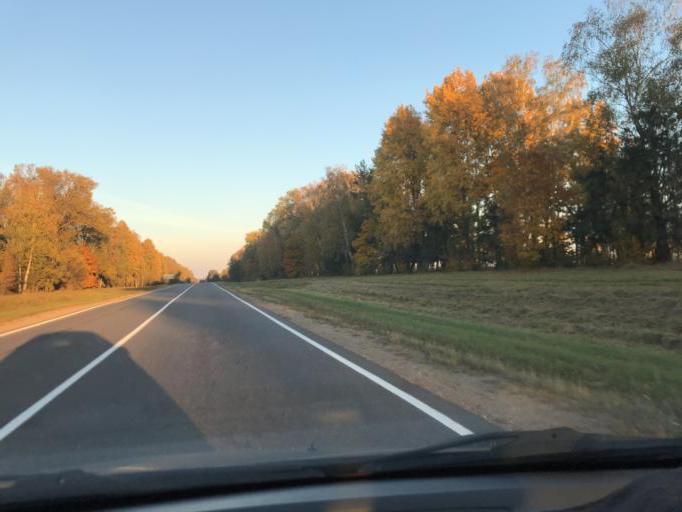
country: BY
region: Minsk
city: Staryya Darohi
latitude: 53.0608
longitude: 28.4877
